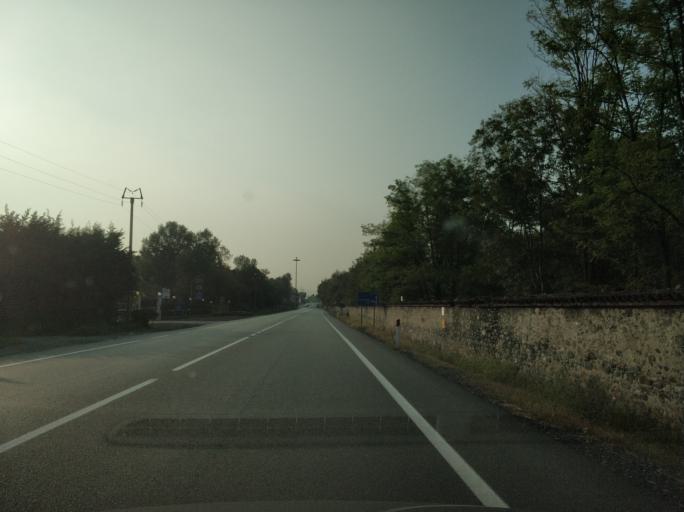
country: IT
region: Piedmont
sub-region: Provincia di Torino
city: Robassomero
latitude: 45.1966
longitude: 7.5601
